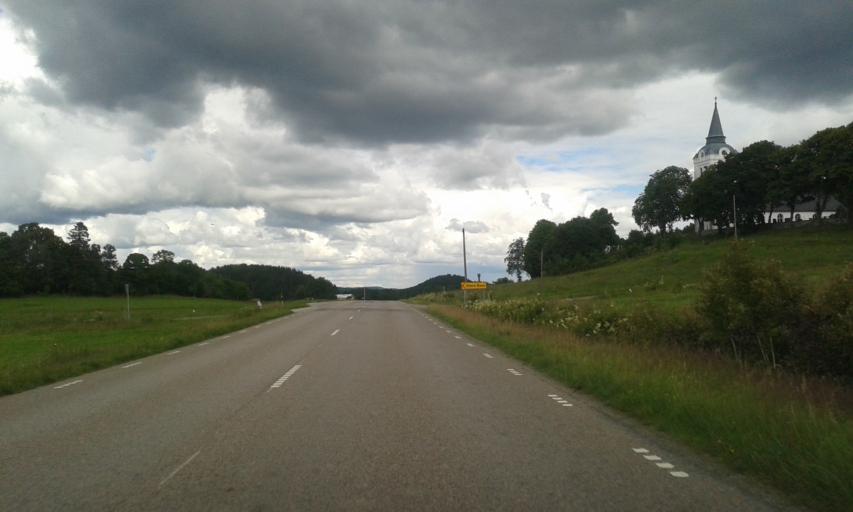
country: SE
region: Vaestra Goetaland
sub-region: Lilla Edets Kommun
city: Lilla Edet
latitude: 58.0888
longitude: 12.1186
